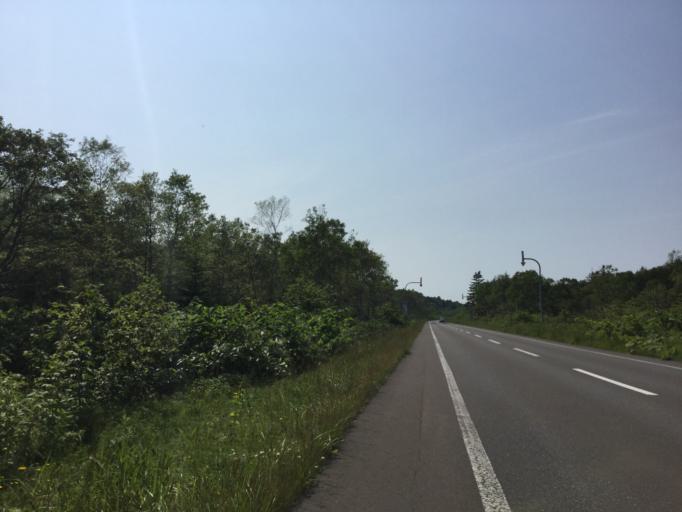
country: JP
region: Hokkaido
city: Makubetsu
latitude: 45.4051
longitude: 142.0216
